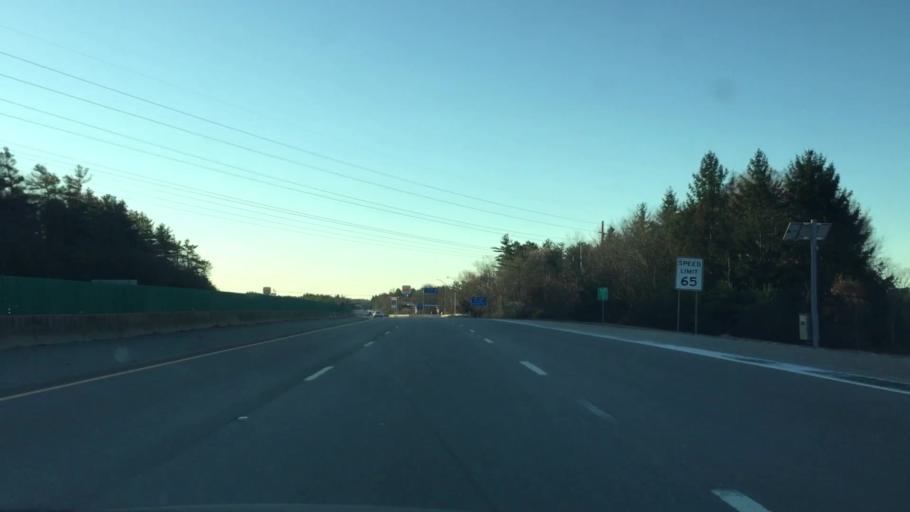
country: US
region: Massachusetts
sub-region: Bristol County
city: Raynham Center
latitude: 41.9597
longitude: -71.0279
